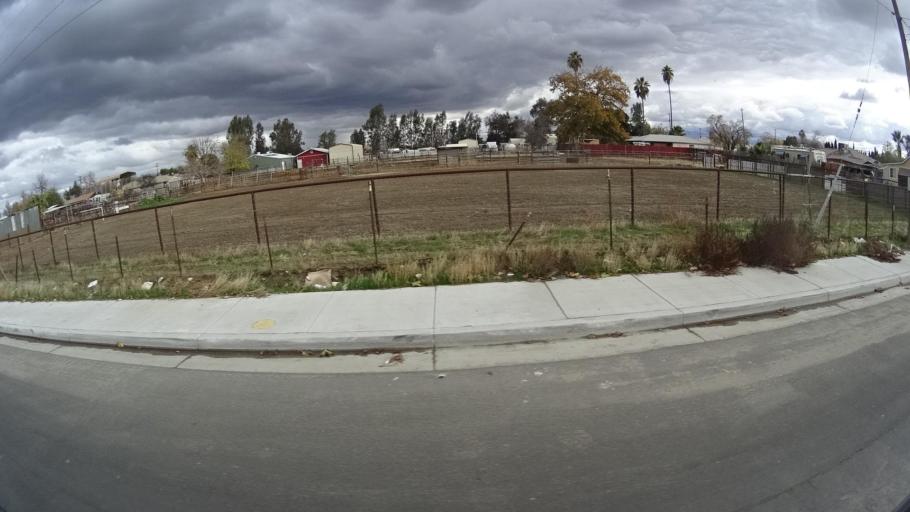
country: US
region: California
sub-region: Kern County
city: Greenfield
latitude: 35.3073
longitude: -118.9943
